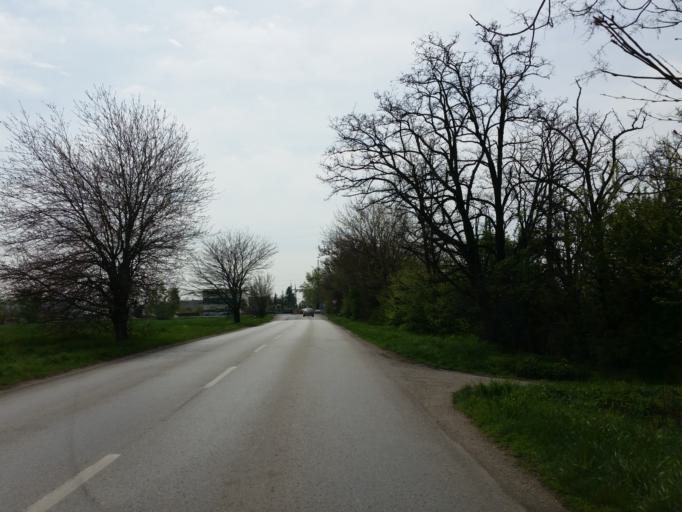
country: SK
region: Trnavsky
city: Leopoldov
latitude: 48.4380
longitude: 17.7677
